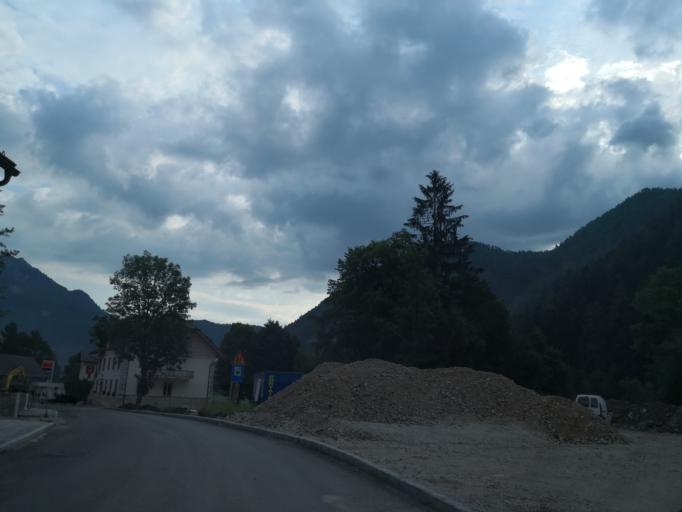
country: SI
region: Jezersko
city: Zgornje Jezersko
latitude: 46.3935
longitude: 14.5002
